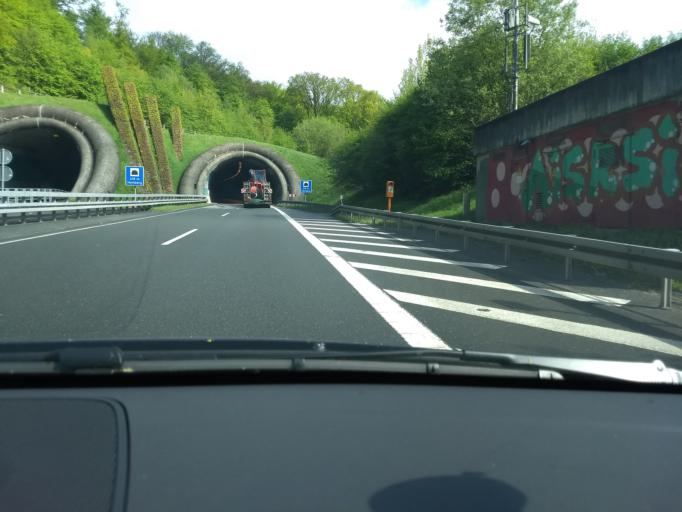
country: DE
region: North Rhine-Westphalia
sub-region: Regierungsbezirk Arnsberg
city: Arnsberg
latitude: 51.3653
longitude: 8.1618
